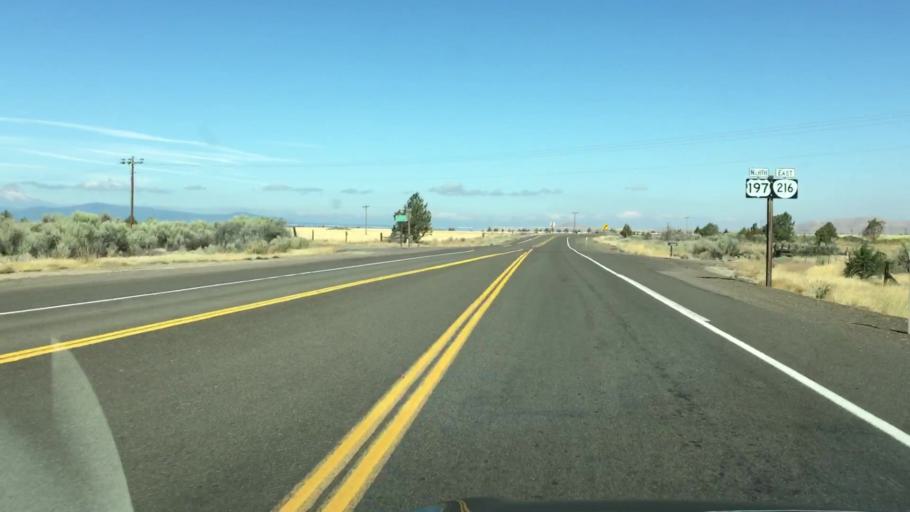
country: US
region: Oregon
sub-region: Wasco County
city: The Dalles
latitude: 45.1713
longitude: -121.1214
